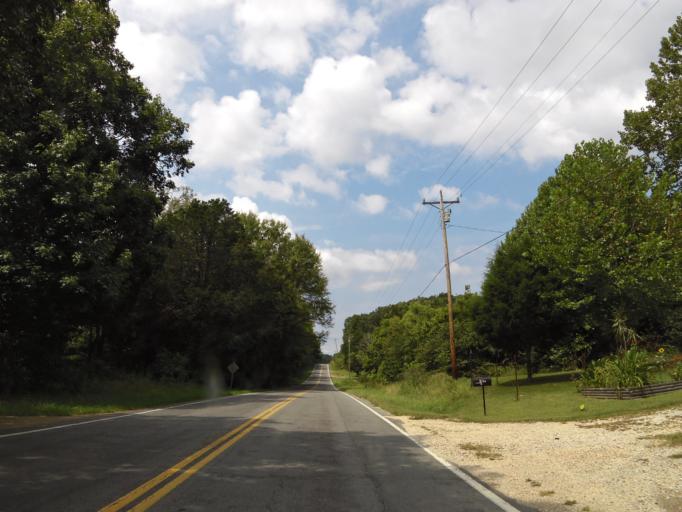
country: US
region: Tennessee
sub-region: Decatur County
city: Mount Carmel
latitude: 35.6185
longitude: -87.9924
